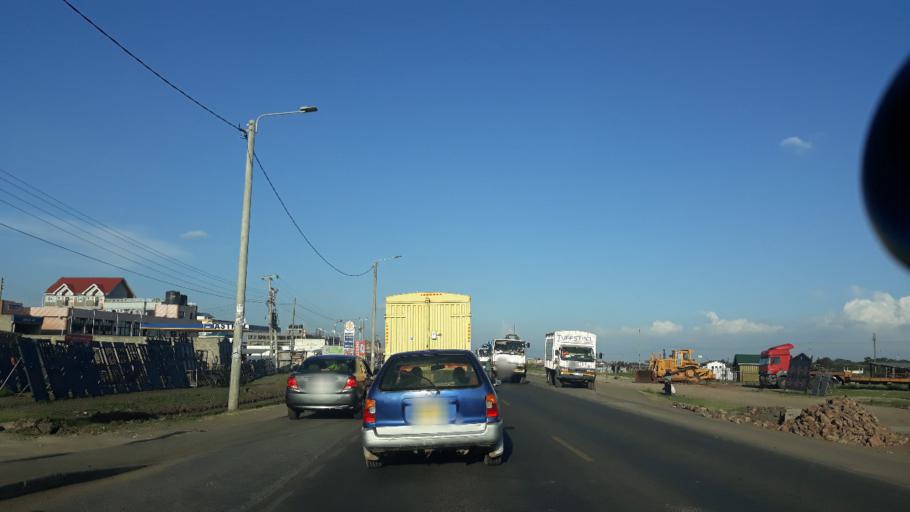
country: KE
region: Nairobi Area
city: Pumwani
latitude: -1.2912
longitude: 36.9464
